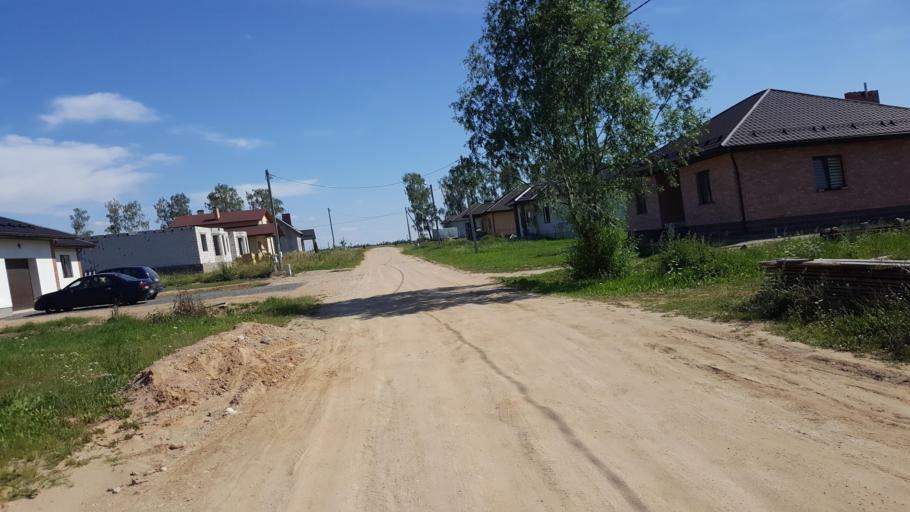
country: BY
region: Brest
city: Charnawchytsy
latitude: 52.2586
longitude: 23.5895
